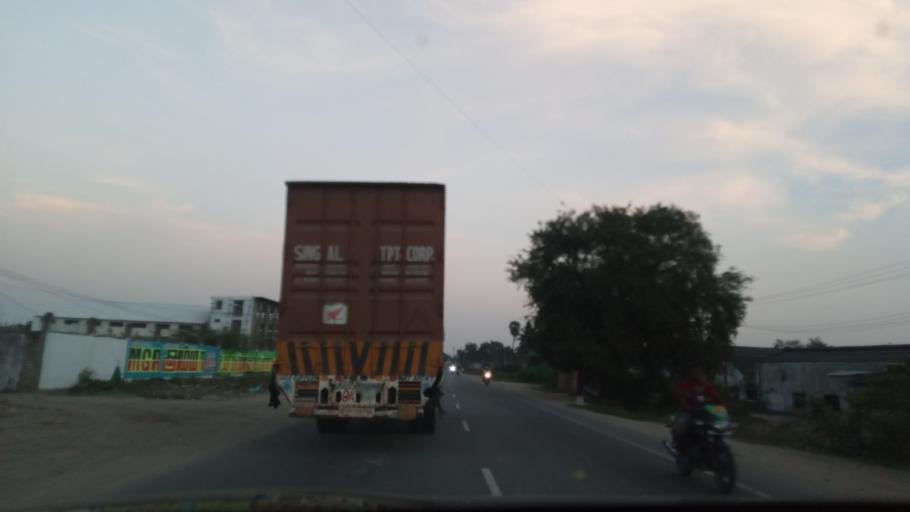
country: IN
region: Tamil Nadu
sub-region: Vellore
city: Walajapet
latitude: 12.9304
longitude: 79.3387
